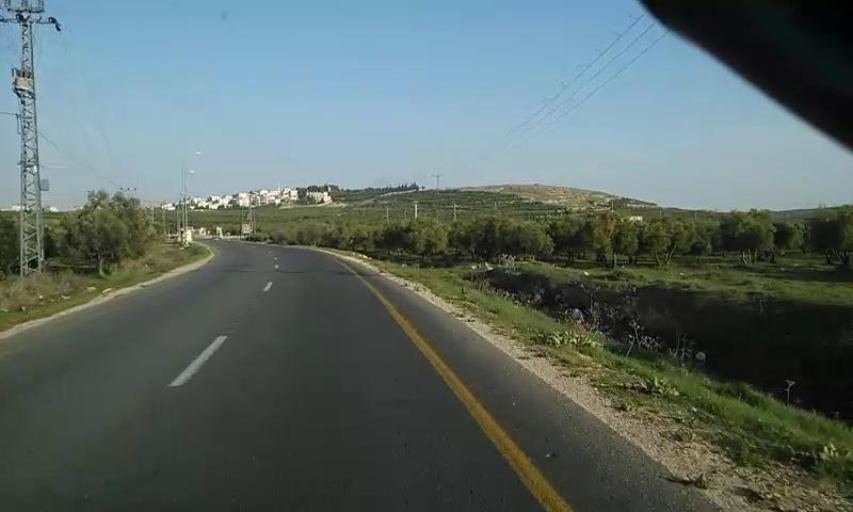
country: PS
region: West Bank
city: Marah Rabbah
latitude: 31.6403
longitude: 35.2014
